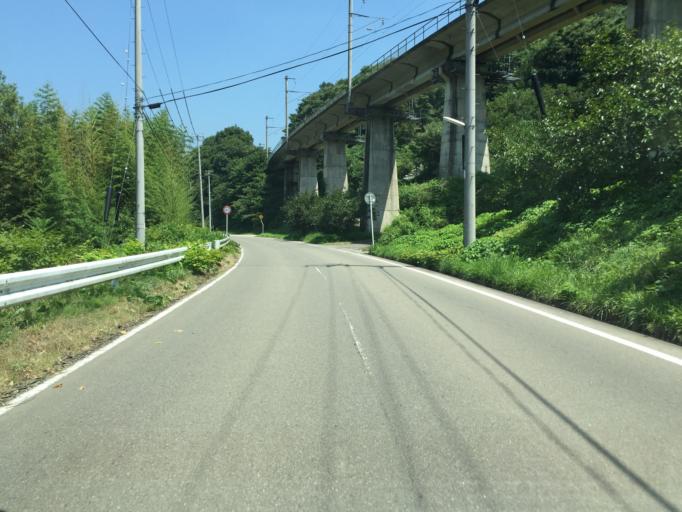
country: JP
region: Fukushima
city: Yanagawamachi-saiwaicho
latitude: 37.8983
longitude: 140.6497
